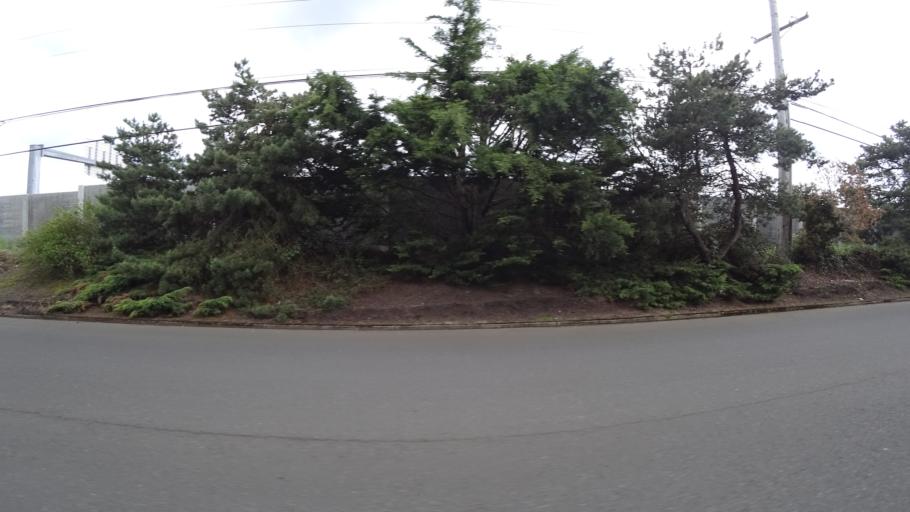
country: US
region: Oregon
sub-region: Washington County
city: Rockcreek
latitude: 45.5463
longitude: -122.8782
